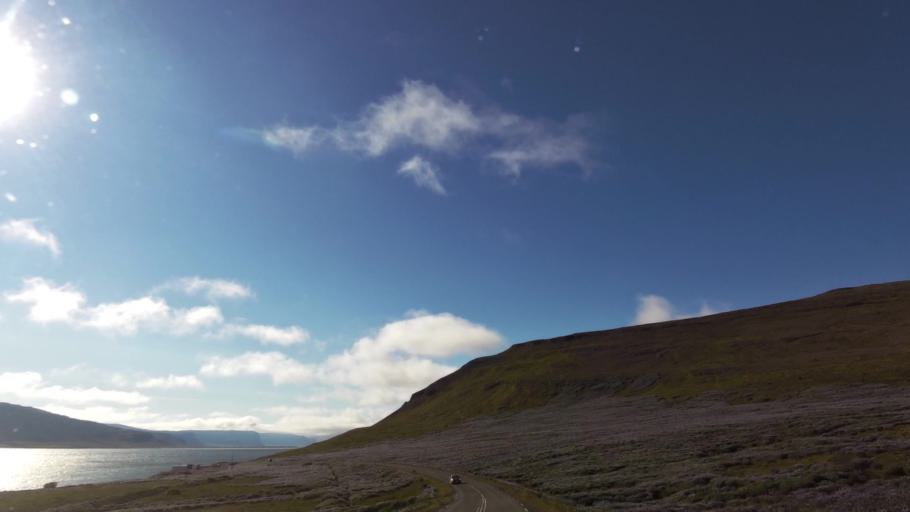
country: IS
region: West
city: Olafsvik
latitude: 65.5421
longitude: -23.8714
